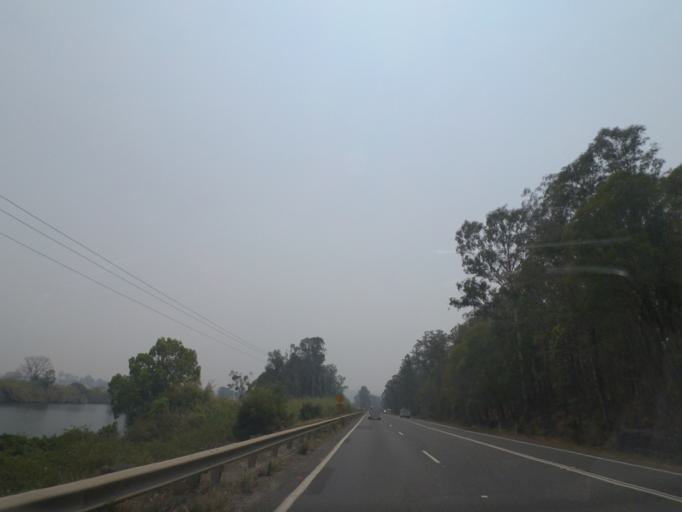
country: AU
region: New South Wales
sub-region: Clarence Valley
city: Maclean
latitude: -29.5577
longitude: 153.1507
